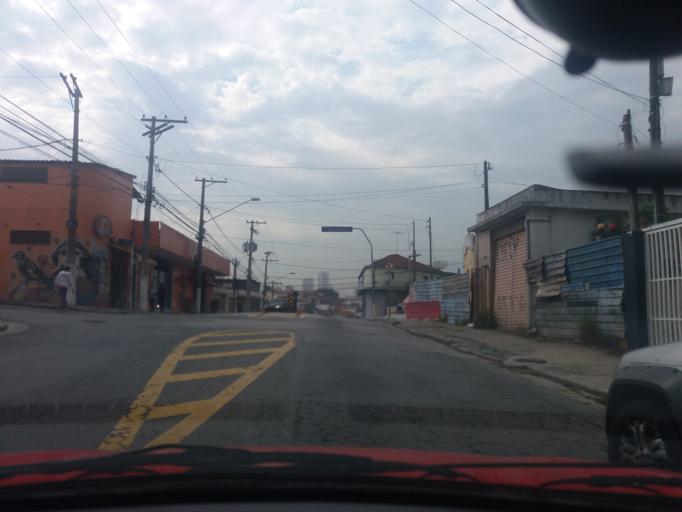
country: BR
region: Sao Paulo
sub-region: Taboao Da Serra
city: Taboao da Serra
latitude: -23.6018
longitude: -46.7401
